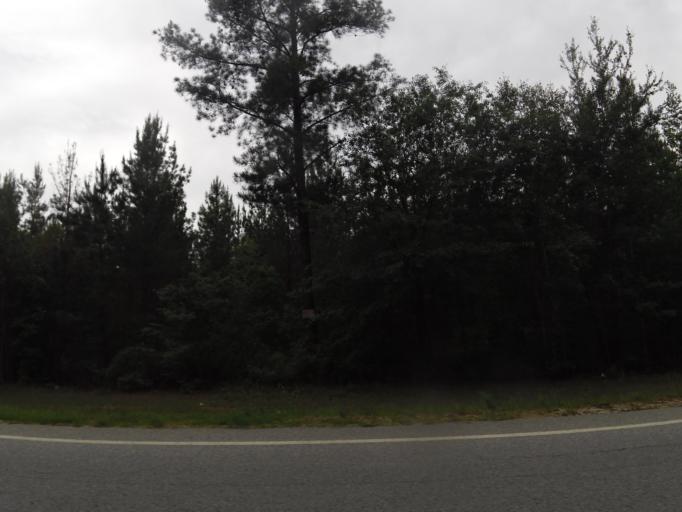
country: US
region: Georgia
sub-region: Emanuel County
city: Twin City
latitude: 32.4599
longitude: -82.2295
